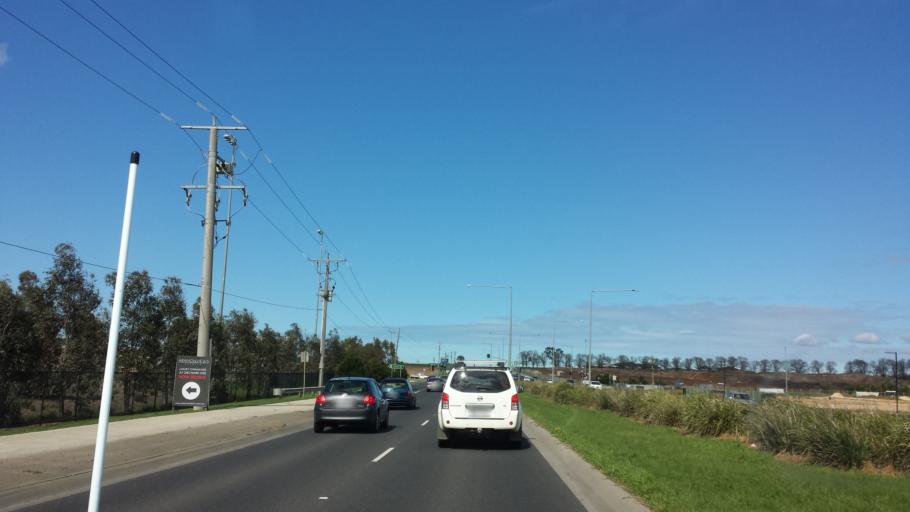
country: AU
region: Victoria
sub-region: Casey
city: Berwick
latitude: -38.0723
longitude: 145.3360
